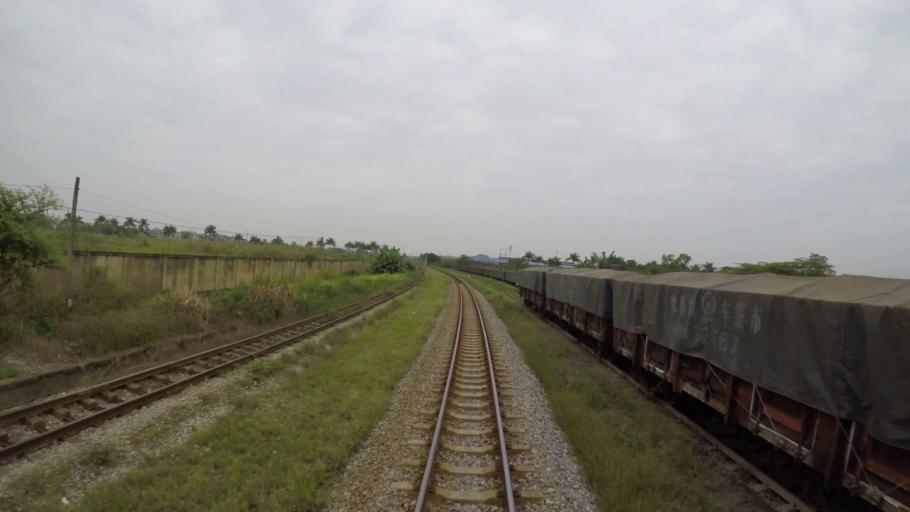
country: VN
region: Hai Phong
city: An Duong
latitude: 20.9056
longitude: 106.5748
